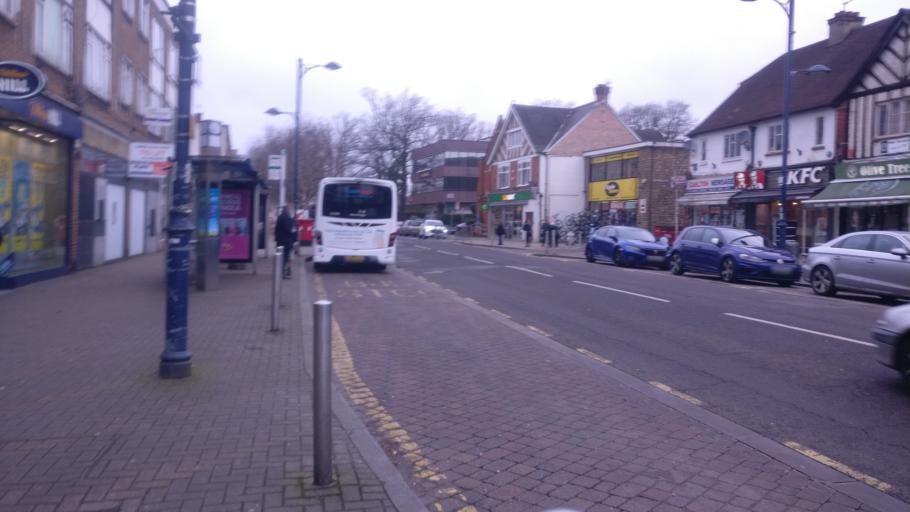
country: GB
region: England
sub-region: Surrey
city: Addlestone
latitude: 51.3714
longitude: -0.4886
